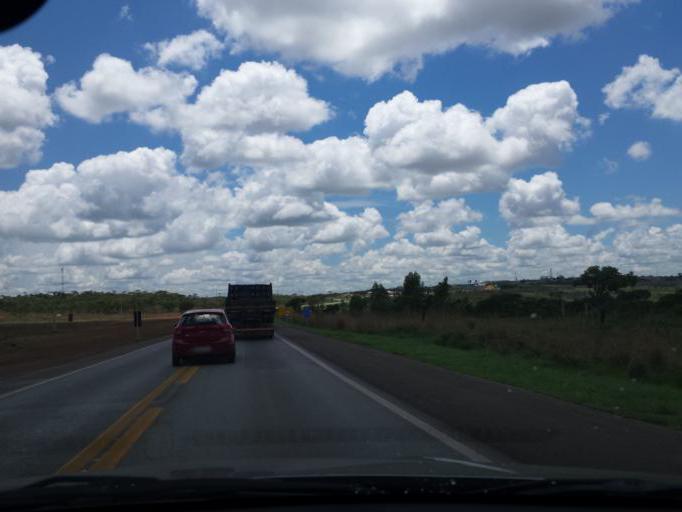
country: BR
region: Goias
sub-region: Cristalina
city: Cristalina
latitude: -16.7306
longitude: -47.6268
